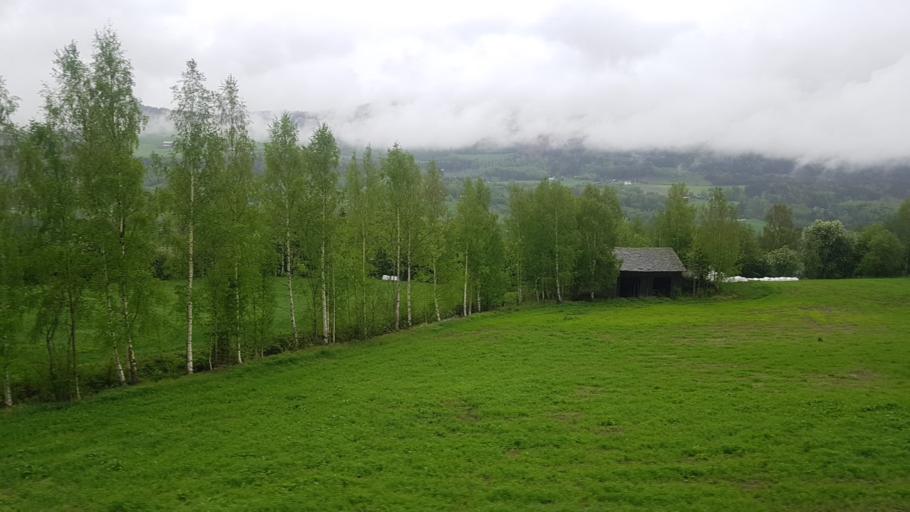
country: NO
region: Oppland
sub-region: Oyer
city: Tretten
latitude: 61.3385
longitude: 10.2875
